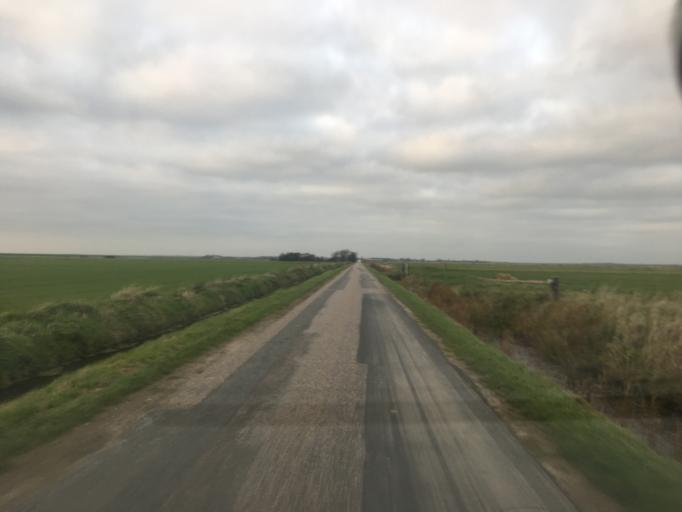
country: DE
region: Schleswig-Holstein
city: Klanxbull
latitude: 54.9326
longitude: 8.6820
